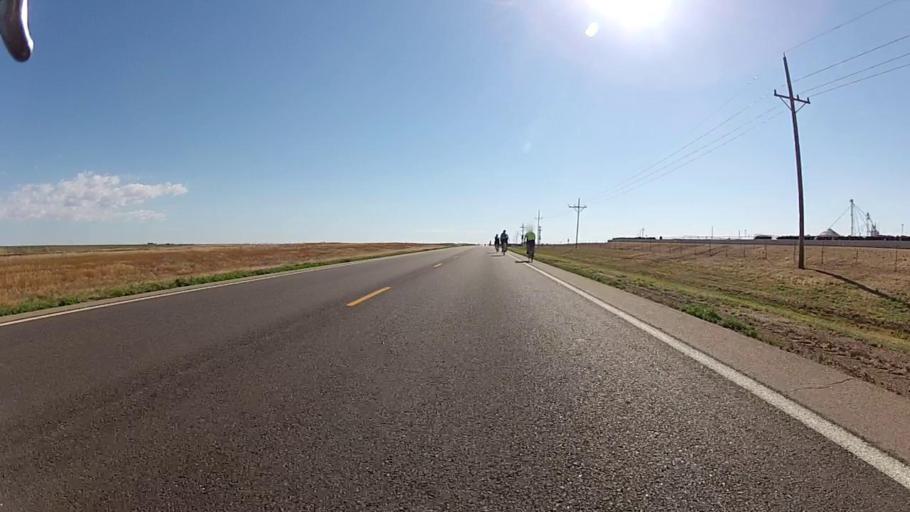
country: US
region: Kansas
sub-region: Gray County
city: Cimarron
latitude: 37.5725
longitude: -100.5346
